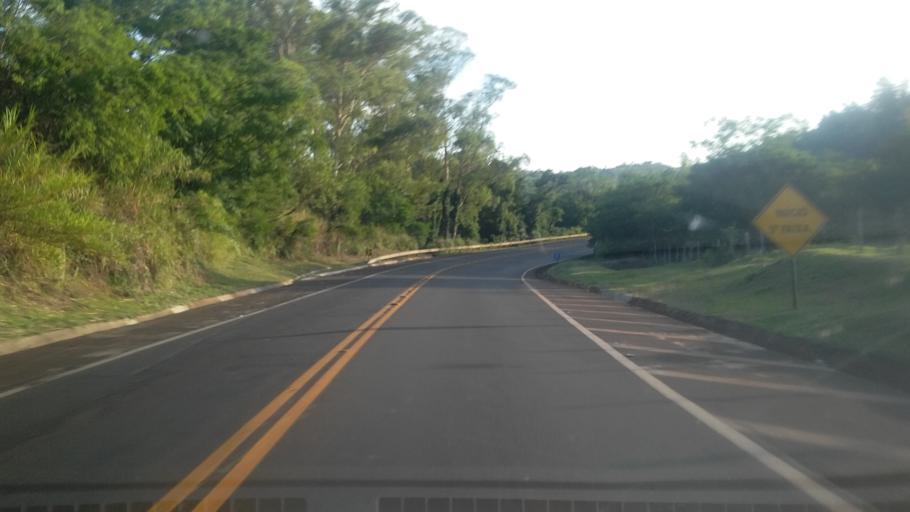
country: BR
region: Parana
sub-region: Assai
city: Assai
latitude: -23.2119
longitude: -50.6676
